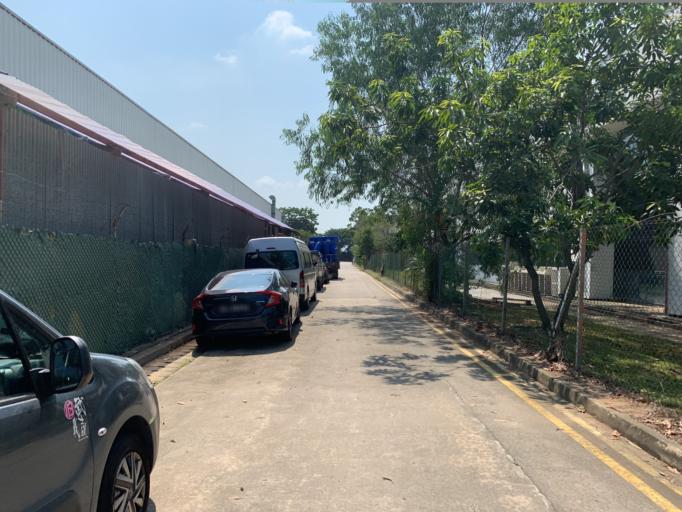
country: MY
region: Johor
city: Johor Bahru
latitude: 1.3062
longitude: 103.6283
